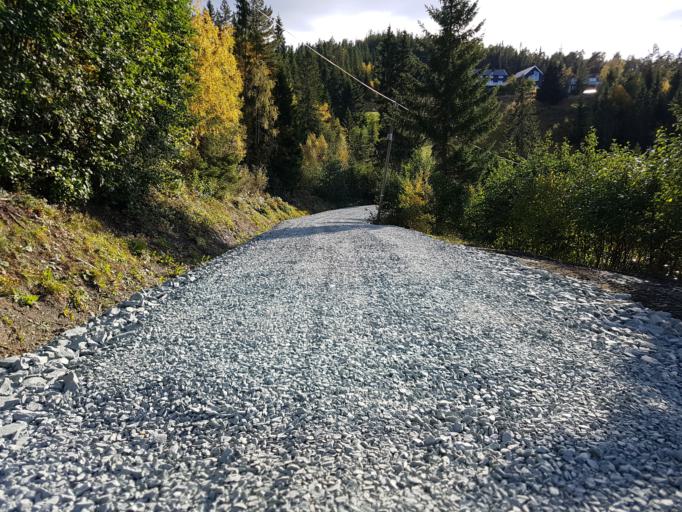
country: NO
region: Sor-Trondelag
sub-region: Klaebu
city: Klaebu
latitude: 63.3419
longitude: 10.5839
